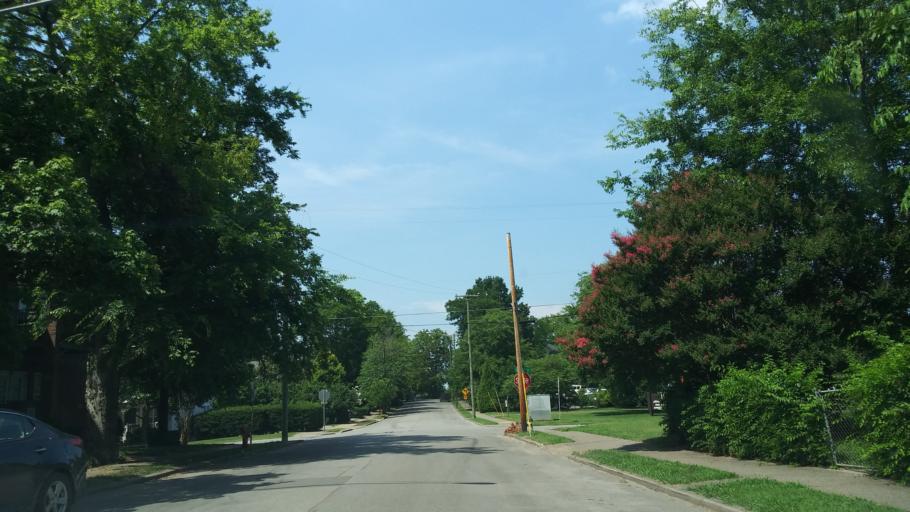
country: US
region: Tennessee
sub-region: Davidson County
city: Nashville
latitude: 36.1469
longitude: -86.8196
